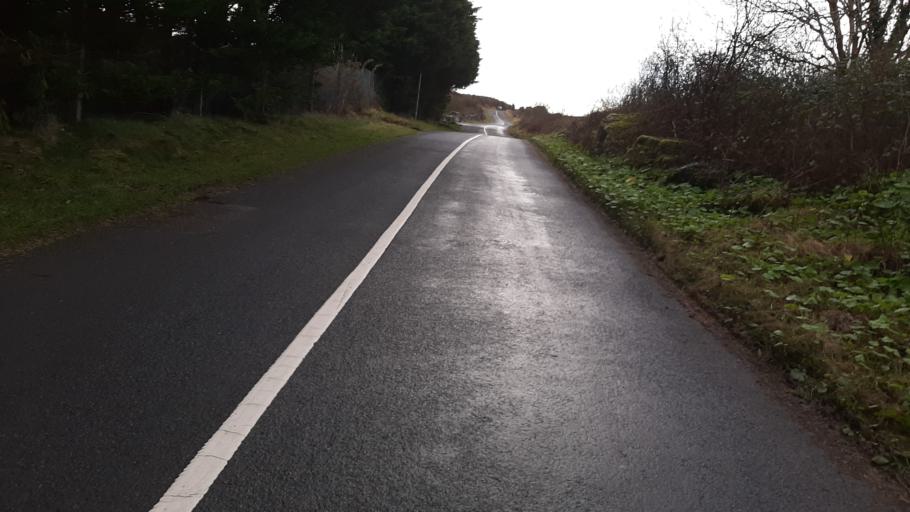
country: IE
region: Connaught
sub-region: County Galway
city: Gaillimh
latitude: 53.3178
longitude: -9.0649
